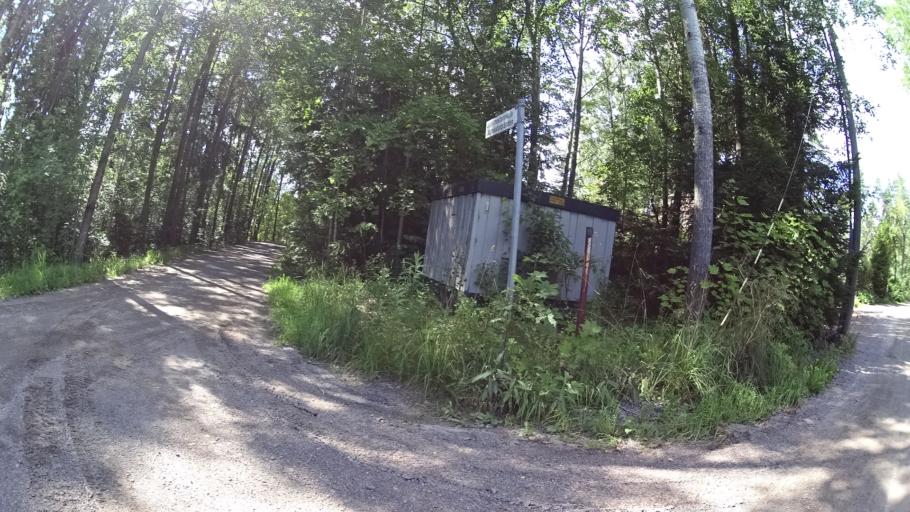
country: FI
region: Uusimaa
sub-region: Helsinki
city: Kauniainen
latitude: 60.2300
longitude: 24.7064
